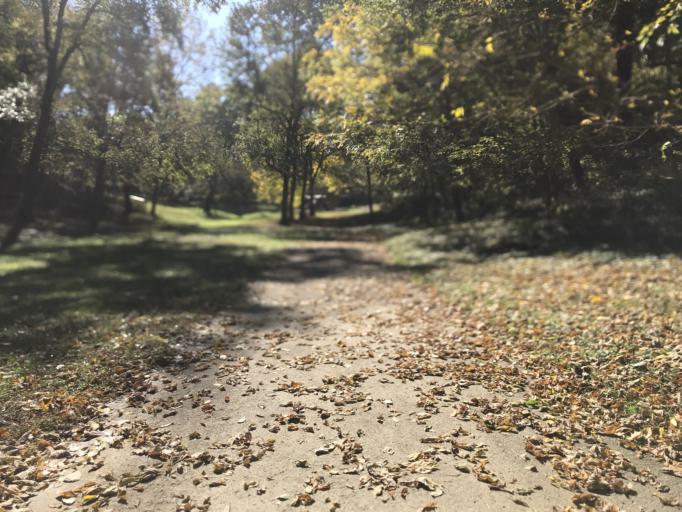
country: US
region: Indiana
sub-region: Clark County
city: Jeffersonville
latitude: 38.2584
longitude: -85.7099
